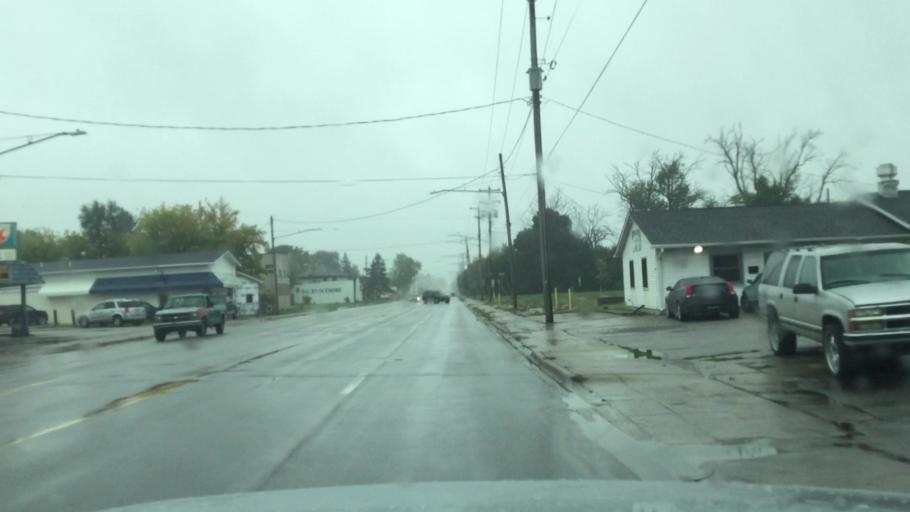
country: US
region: Michigan
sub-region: Saginaw County
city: Buena Vista
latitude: 43.4083
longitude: -83.9173
